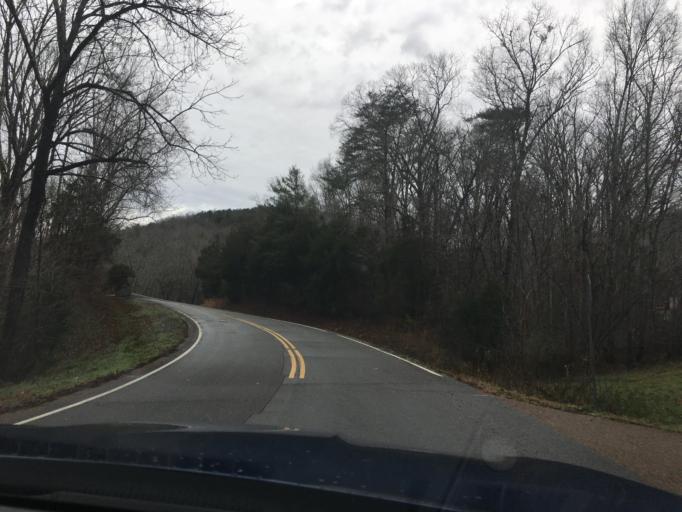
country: US
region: Tennessee
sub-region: McMinn County
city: Englewood
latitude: 35.3567
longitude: -84.4197
